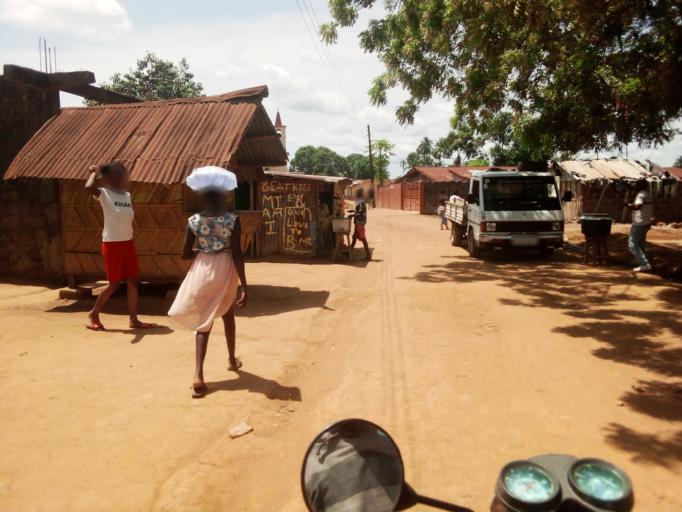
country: SL
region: Western Area
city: Waterloo
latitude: 8.3303
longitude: -13.0753
